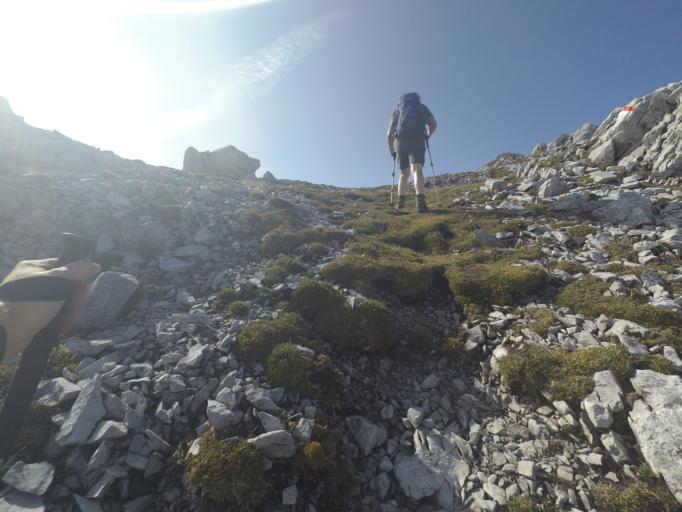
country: AT
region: Salzburg
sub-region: Politischer Bezirk Sankt Johann im Pongau
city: Kleinarl
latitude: 47.2179
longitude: 13.4042
